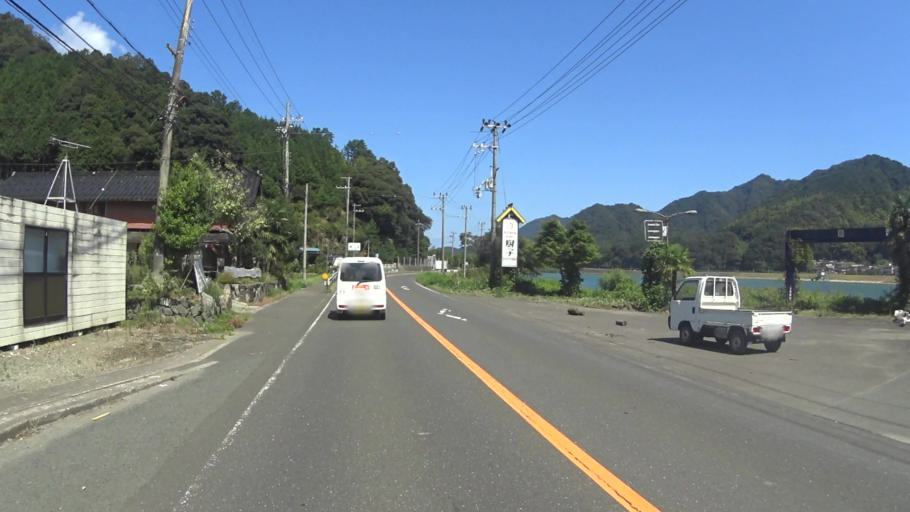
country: JP
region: Kyoto
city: Maizuru
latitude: 35.4769
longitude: 135.2775
